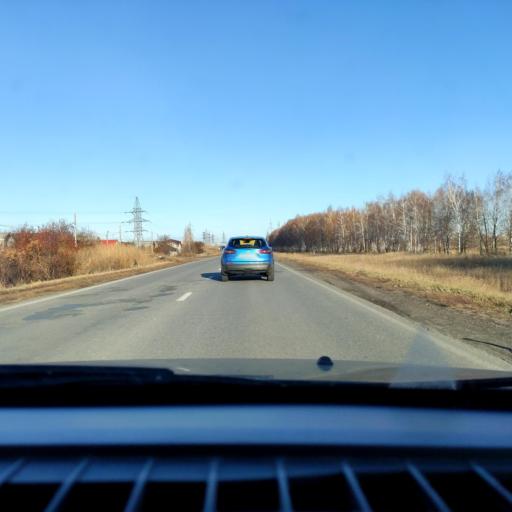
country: RU
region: Samara
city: Tol'yatti
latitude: 53.5810
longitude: 49.3357
